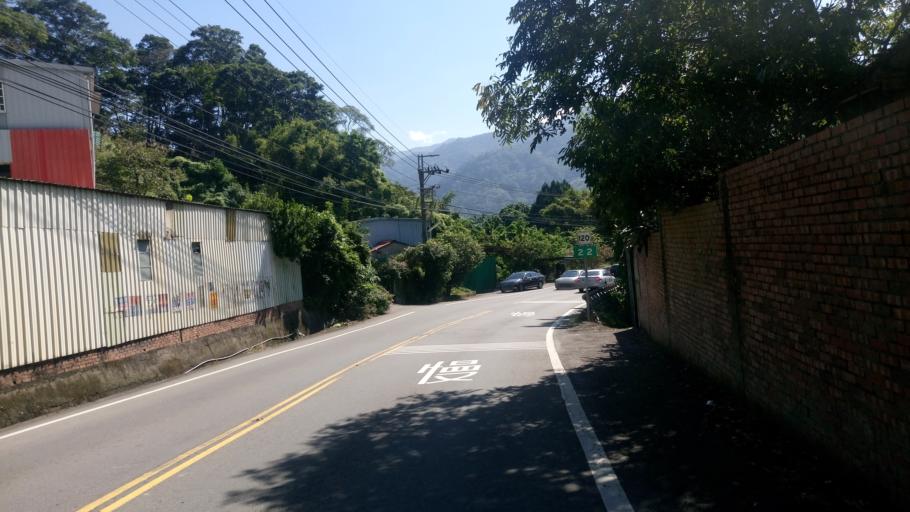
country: TW
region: Taiwan
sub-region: Hsinchu
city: Zhubei
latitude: 24.7169
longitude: 121.1629
